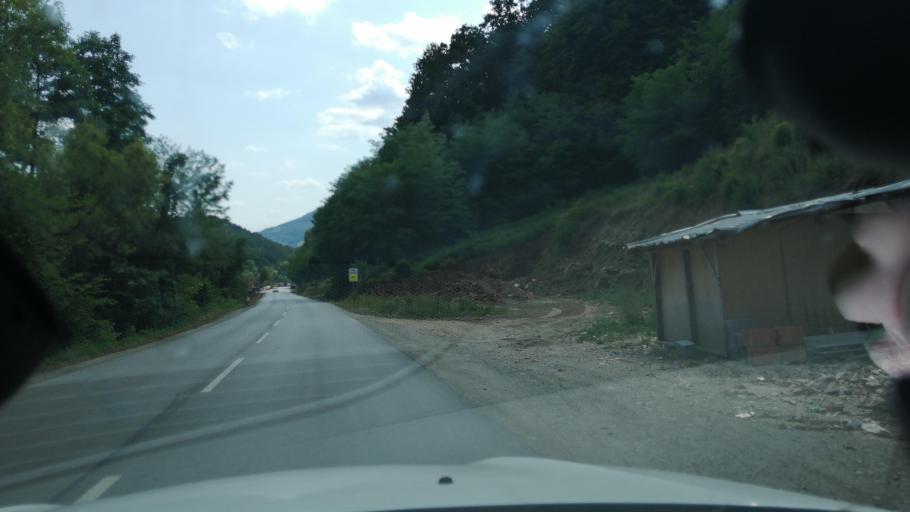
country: RS
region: Central Serbia
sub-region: Moravicki Okrug
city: Ivanjica
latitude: 43.6114
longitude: 20.2357
